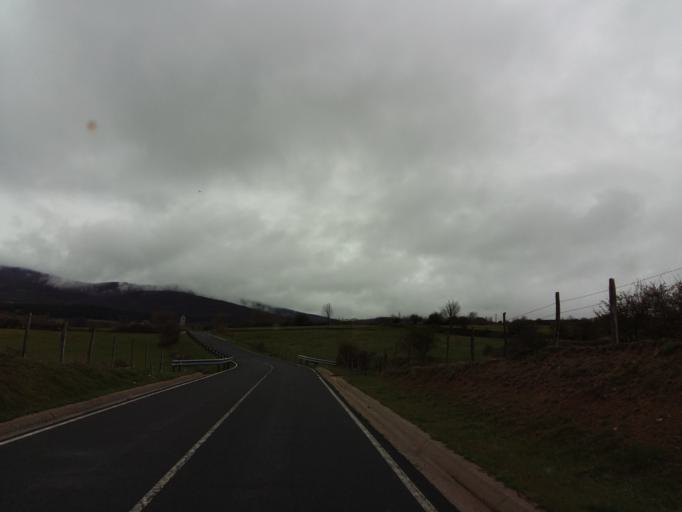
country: ES
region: Cantabria
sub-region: Provincia de Cantabria
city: Villaescusa
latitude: 42.9360
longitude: -4.2086
